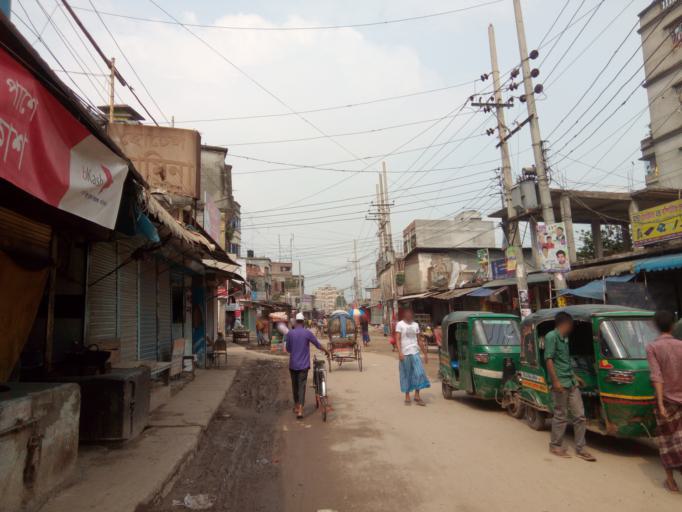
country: BD
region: Dhaka
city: Paltan
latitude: 23.7308
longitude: 90.4414
